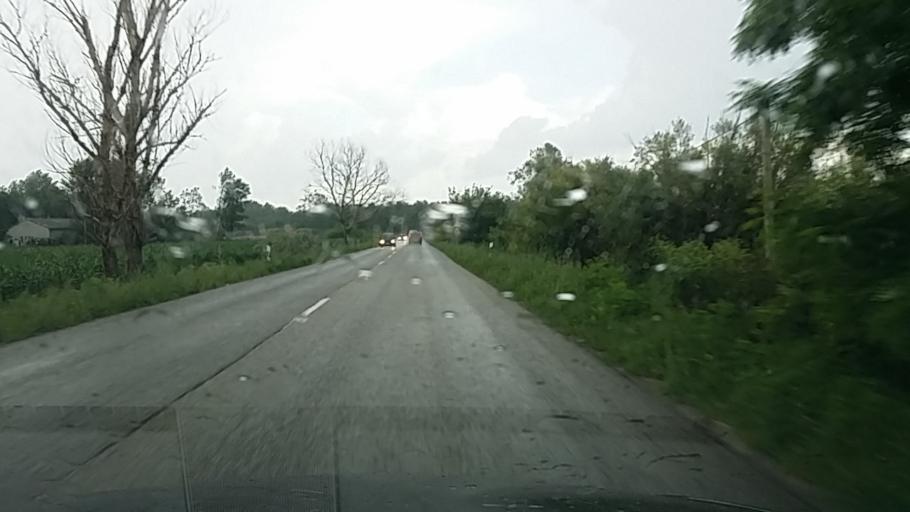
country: HU
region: Pest
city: Ocsa
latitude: 47.3012
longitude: 19.2616
